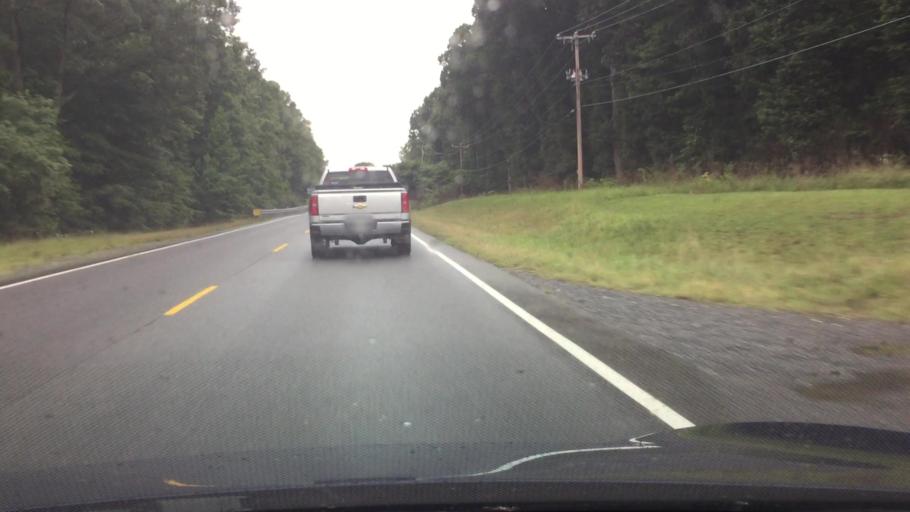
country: US
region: Virginia
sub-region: City of Bedford
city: Bedford
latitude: 37.3633
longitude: -79.4470
